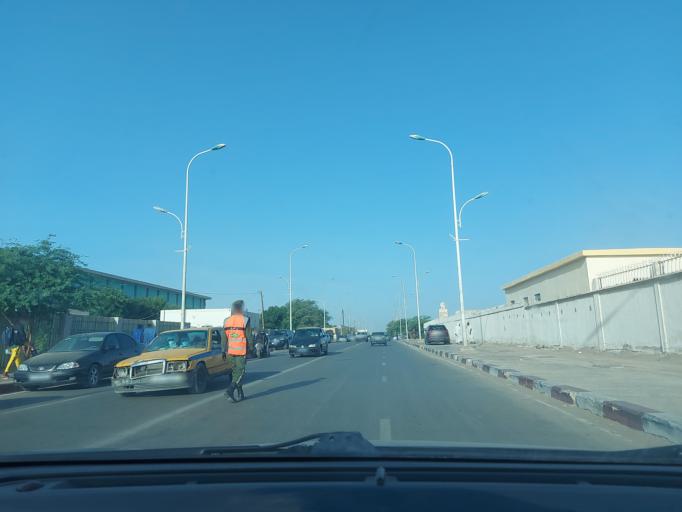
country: MR
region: Nouakchott
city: Nouakchott
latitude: 18.0865
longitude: -15.9873
